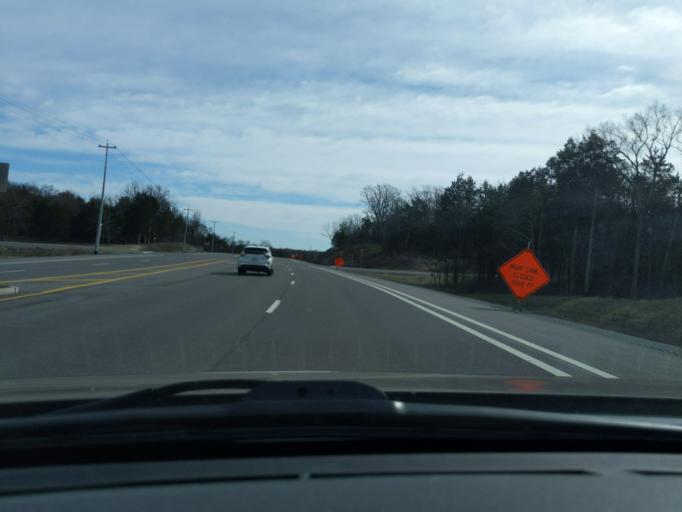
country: US
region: Tennessee
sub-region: Wilson County
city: Mount Juliet
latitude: 36.1878
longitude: -86.4708
